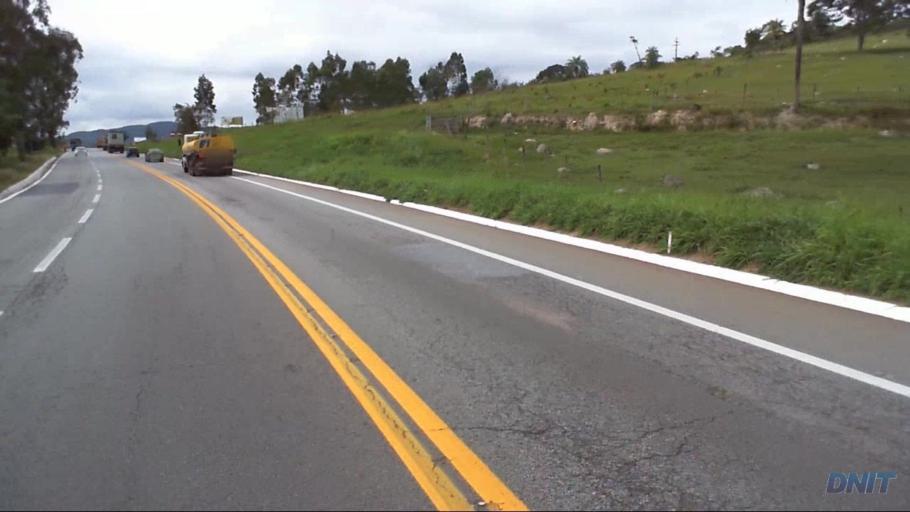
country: BR
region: Minas Gerais
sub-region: Caete
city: Caete
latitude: -19.7259
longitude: -43.5879
